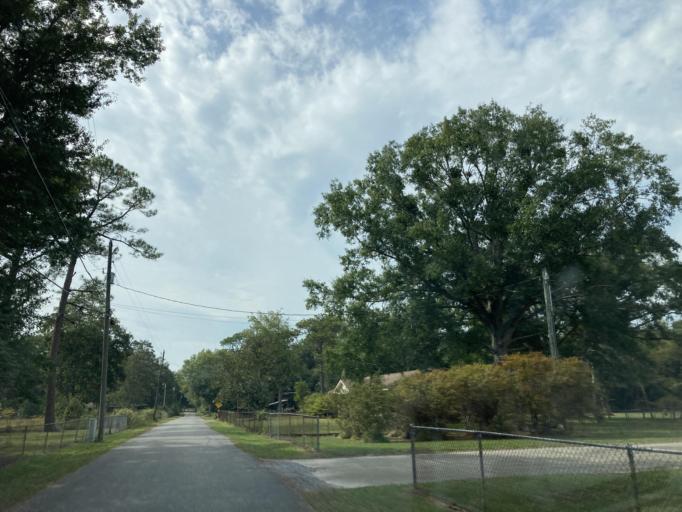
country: US
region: Mississippi
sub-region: Jackson County
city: Saint Martin
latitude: 30.4666
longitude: -88.8552
